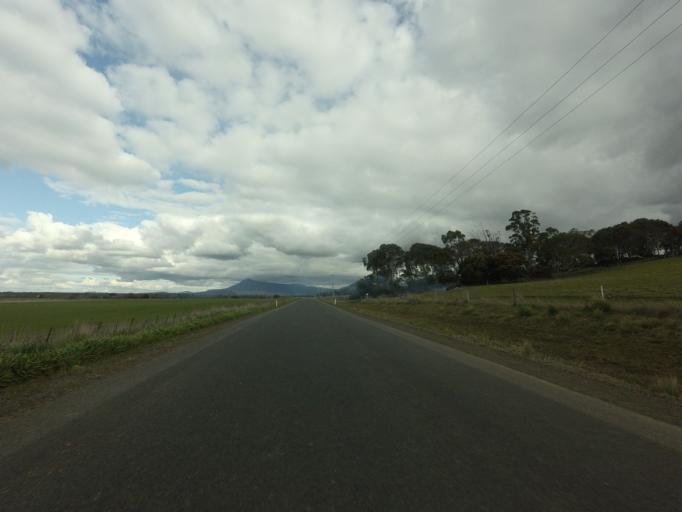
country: AU
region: Tasmania
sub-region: Northern Midlands
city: Longford
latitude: -41.7779
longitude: 147.0961
